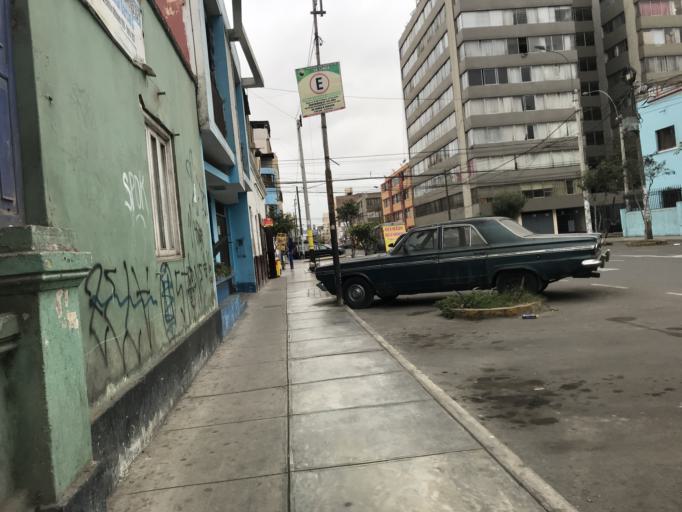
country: PE
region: Lima
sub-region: Lima
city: San Isidro
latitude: -12.0806
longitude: -77.0374
